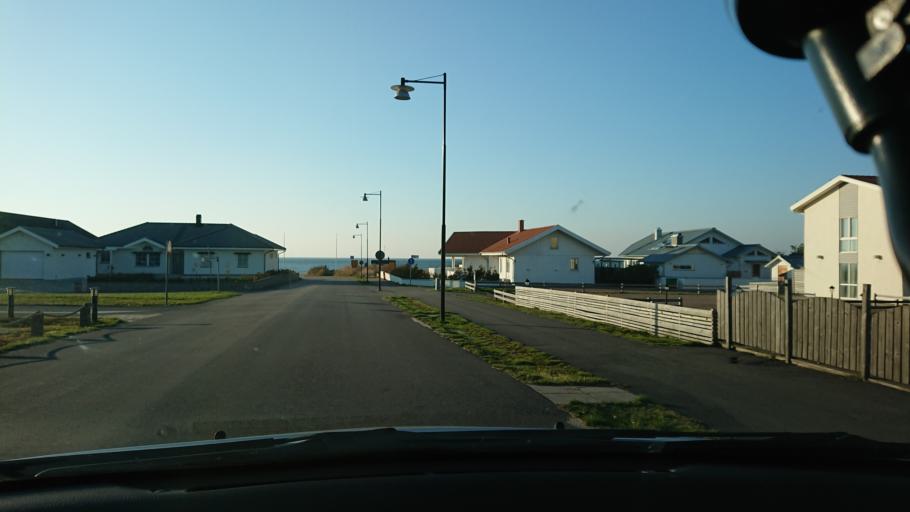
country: SE
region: Halland
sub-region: Laholms Kommun
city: Mellbystrand
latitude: 56.4620
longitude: 12.9174
